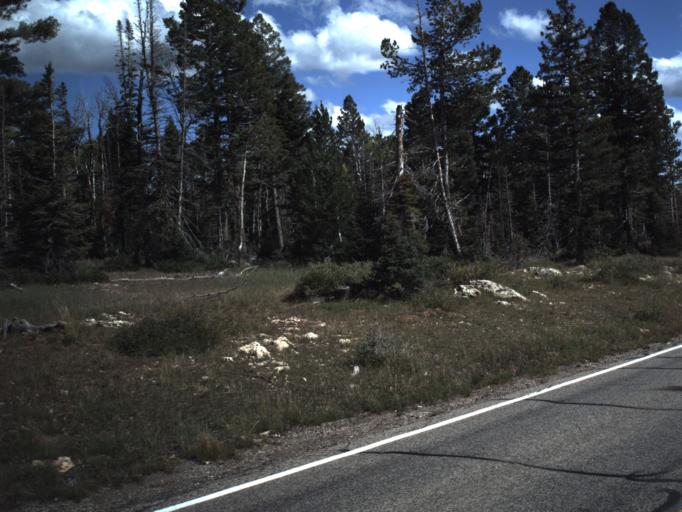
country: US
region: Utah
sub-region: Iron County
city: Parowan
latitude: 37.5292
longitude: -112.7644
